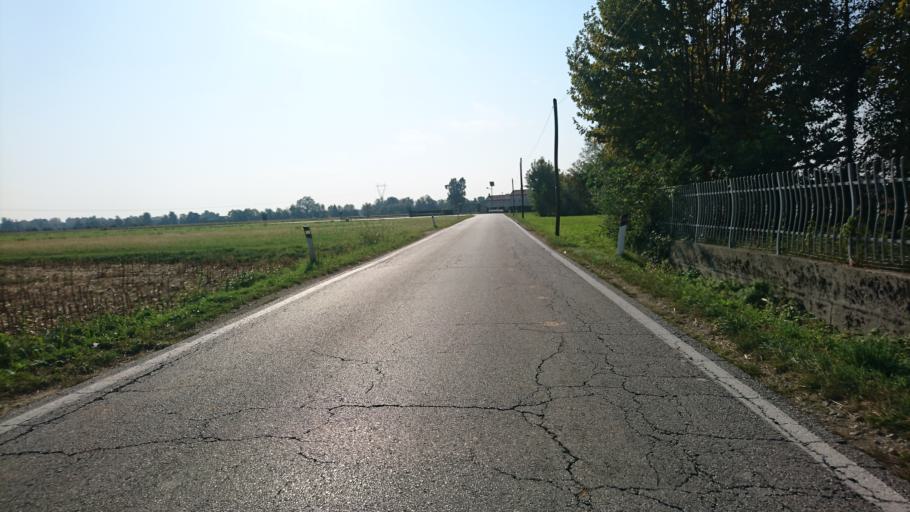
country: IT
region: Veneto
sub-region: Provincia di Padova
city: Gazzo
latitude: 45.5964
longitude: 11.6930
